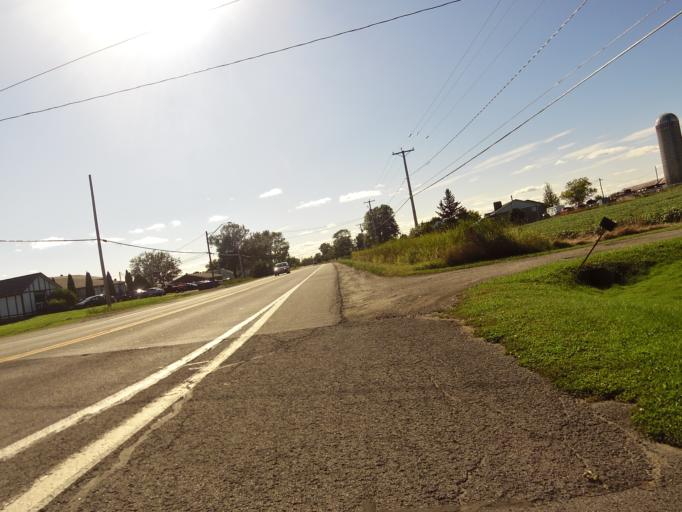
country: CA
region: Quebec
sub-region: Outaouais
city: Gatineau
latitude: 45.5202
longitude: -75.5040
